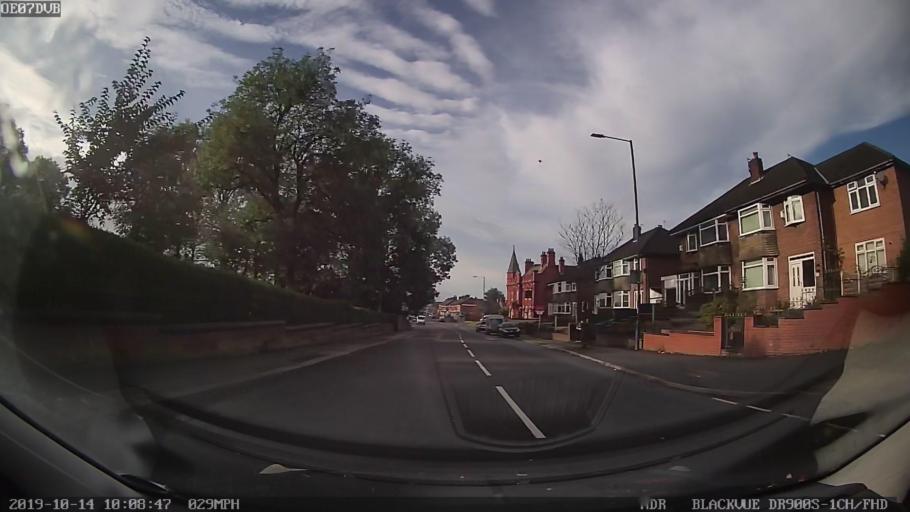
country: GB
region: England
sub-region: Manchester
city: Blackley
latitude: 53.5163
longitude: -2.1902
